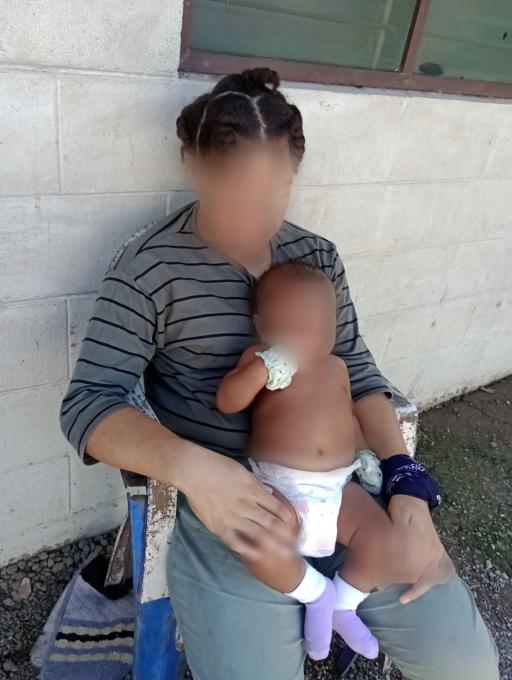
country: PG
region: National Capital
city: Port Moresby
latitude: -9.4712
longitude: 147.2077
